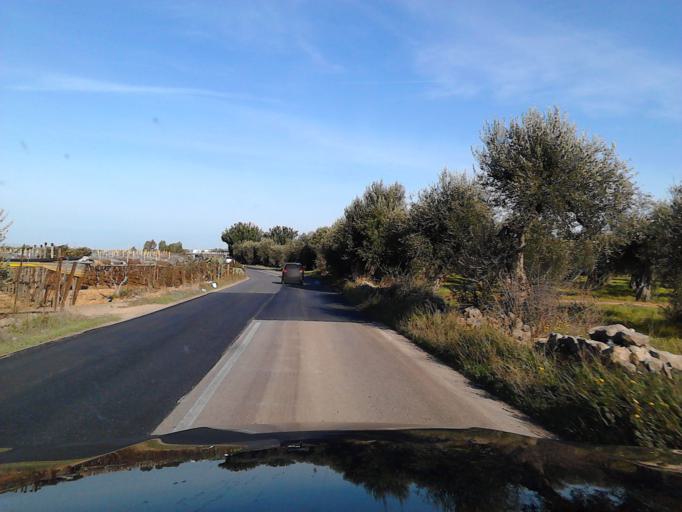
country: IT
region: Apulia
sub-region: Provincia di Bari
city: Cellamare
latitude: 41.0117
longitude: 16.9621
